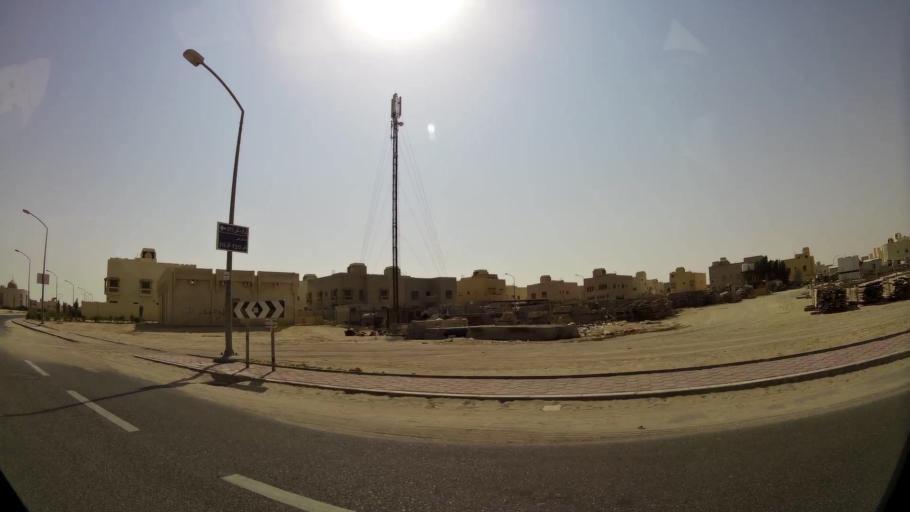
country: KW
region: Al Ahmadi
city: Al Wafrah
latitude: 28.8095
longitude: 48.0548
